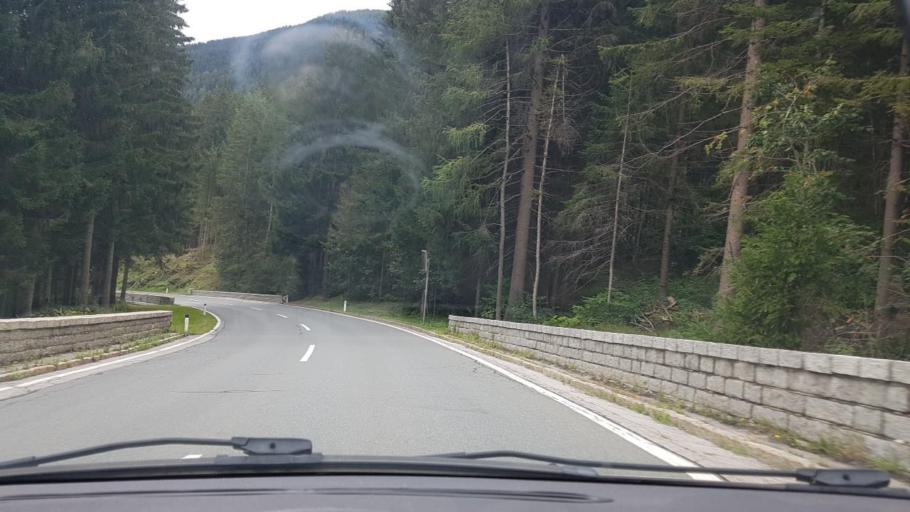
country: AT
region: Carinthia
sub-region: Politischer Bezirk Spittal an der Drau
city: Winklern
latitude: 46.8654
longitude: 12.8703
